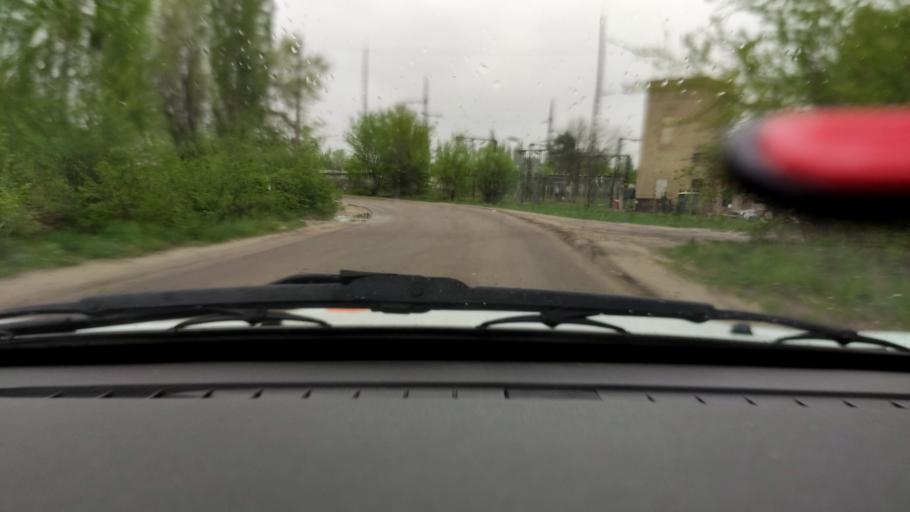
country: RU
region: Voronezj
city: Strelitsa
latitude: 51.6041
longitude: 38.9012
